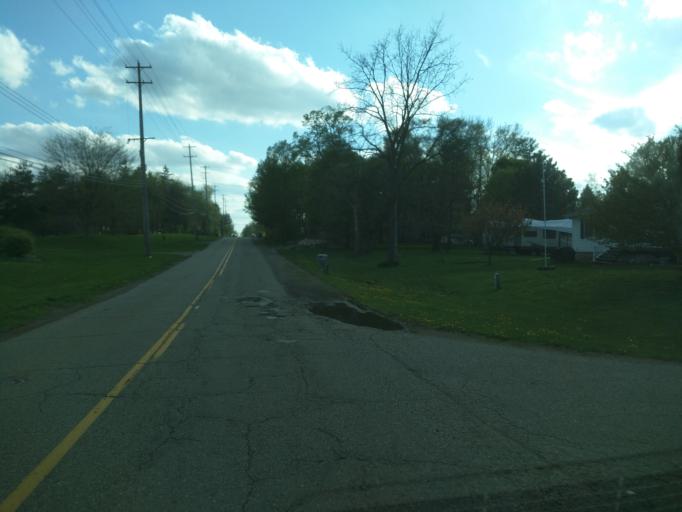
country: US
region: Michigan
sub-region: Eaton County
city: Waverly
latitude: 42.7014
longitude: -84.6199
